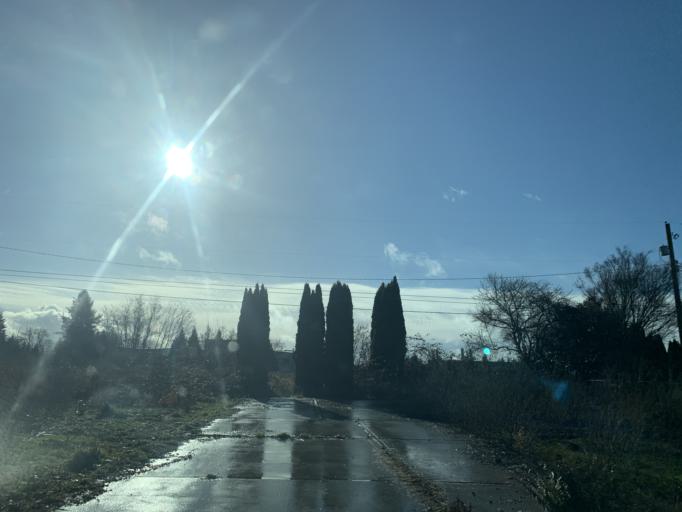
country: US
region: Washington
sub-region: Pierce County
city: Fife Heights
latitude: 47.2484
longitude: -122.3484
